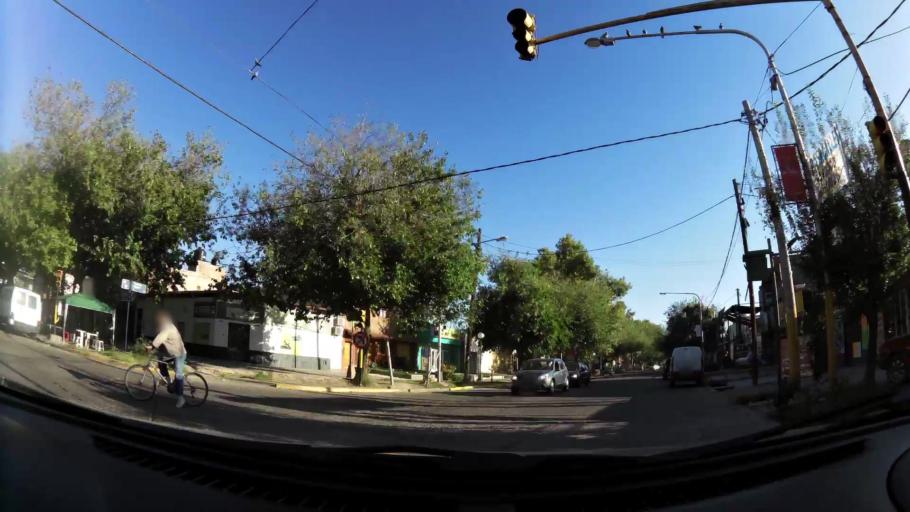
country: AR
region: Mendoza
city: Las Heras
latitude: -32.8664
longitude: -68.8226
